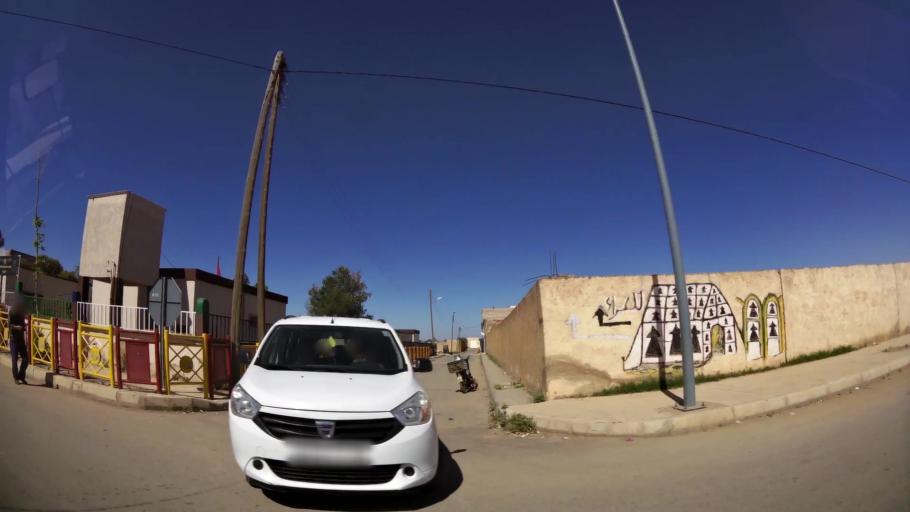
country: MA
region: Oriental
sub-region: Oujda-Angad
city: Oujda
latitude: 34.7096
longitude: -1.8606
